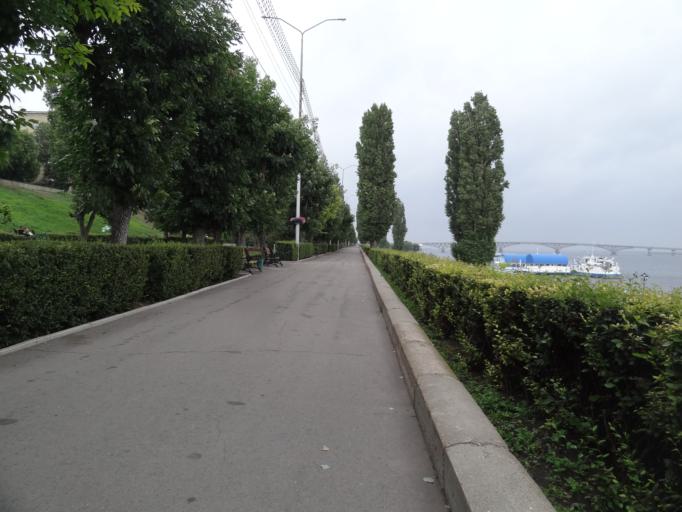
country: RU
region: Saratov
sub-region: Saratovskiy Rayon
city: Saratov
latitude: 51.5243
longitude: 46.0450
